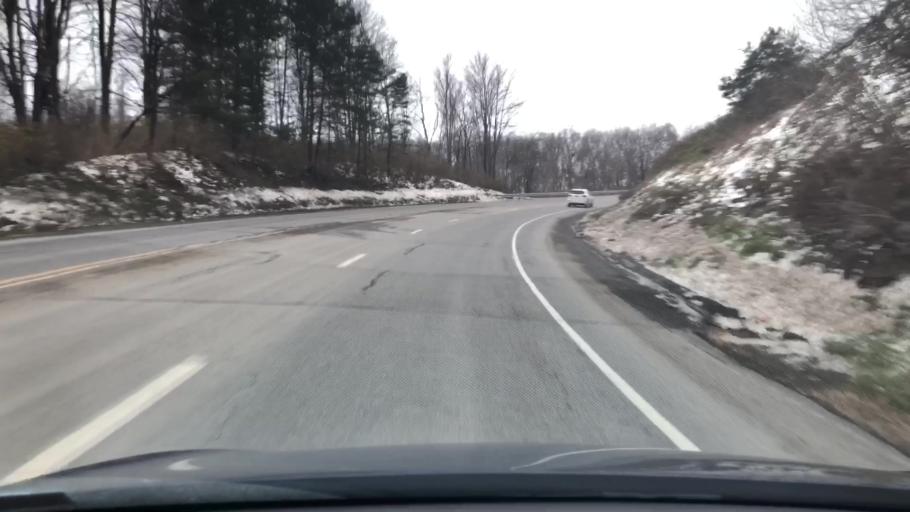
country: US
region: Pennsylvania
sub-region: Jefferson County
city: Brookville
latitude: 41.1124
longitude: -79.2050
